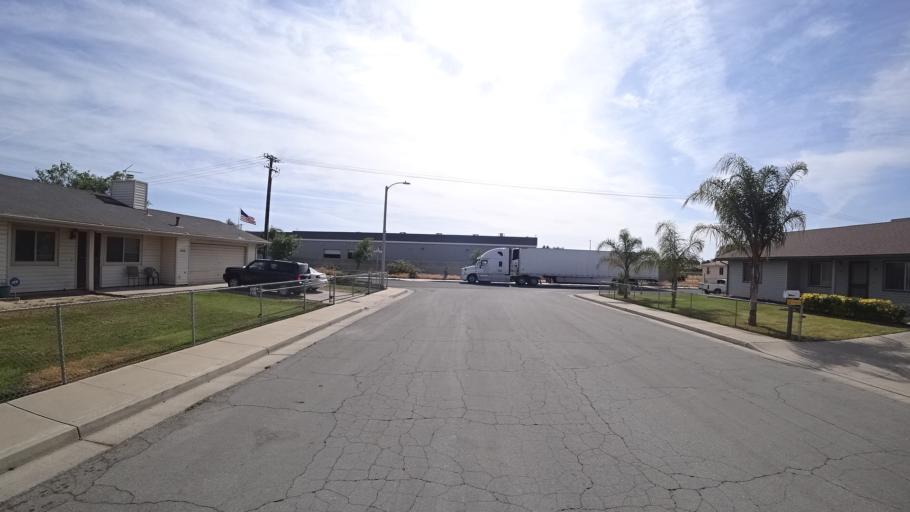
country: US
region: California
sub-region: Kings County
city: Hanford
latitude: 36.3192
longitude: -119.6621
